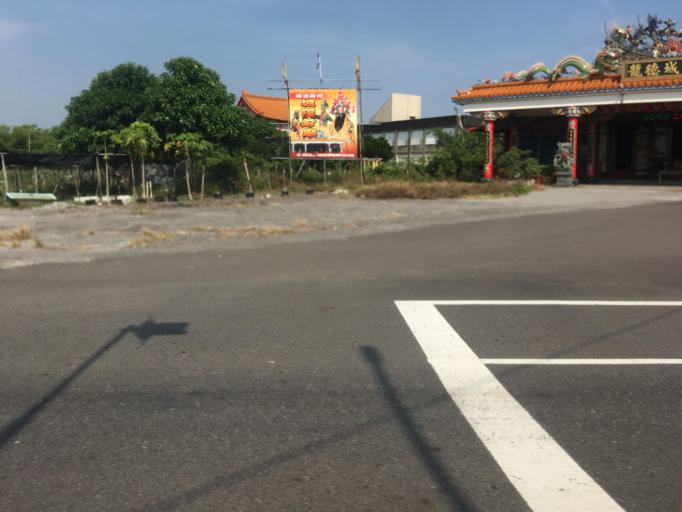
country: TW
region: Taiwan
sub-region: Yilan
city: Yilan
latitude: 24.6394
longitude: 121.8340
